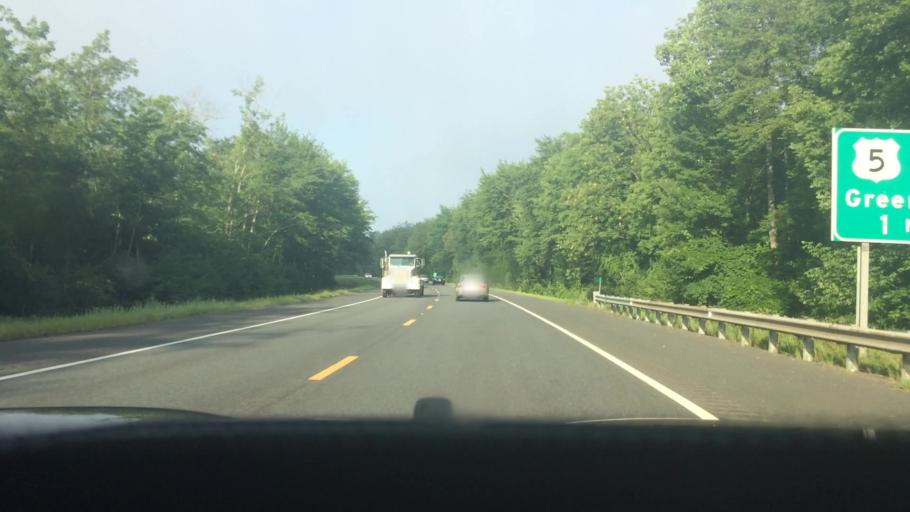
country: US
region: Massachusetts
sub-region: Franklin County
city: Turners Falls
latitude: 42.6143
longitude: -72.5655
